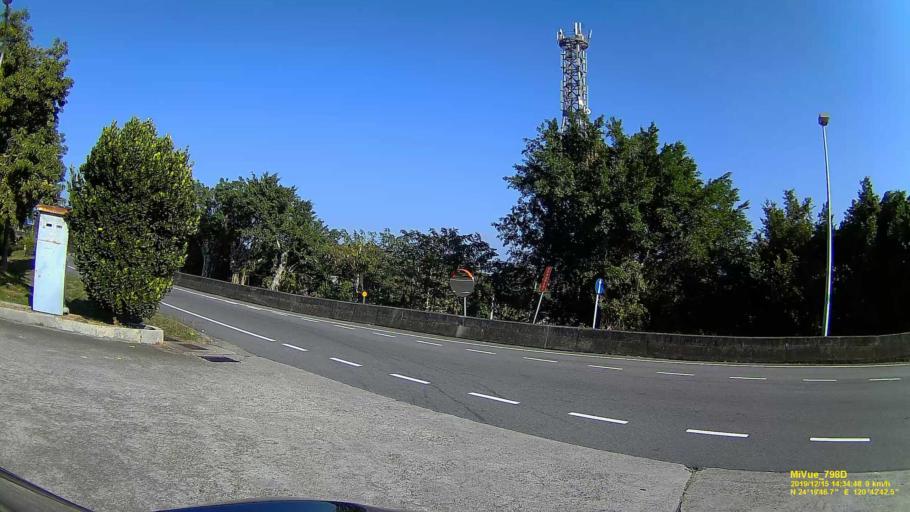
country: TW
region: Taiwan
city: Fengyuan
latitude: 24.3297
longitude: 120.7119
